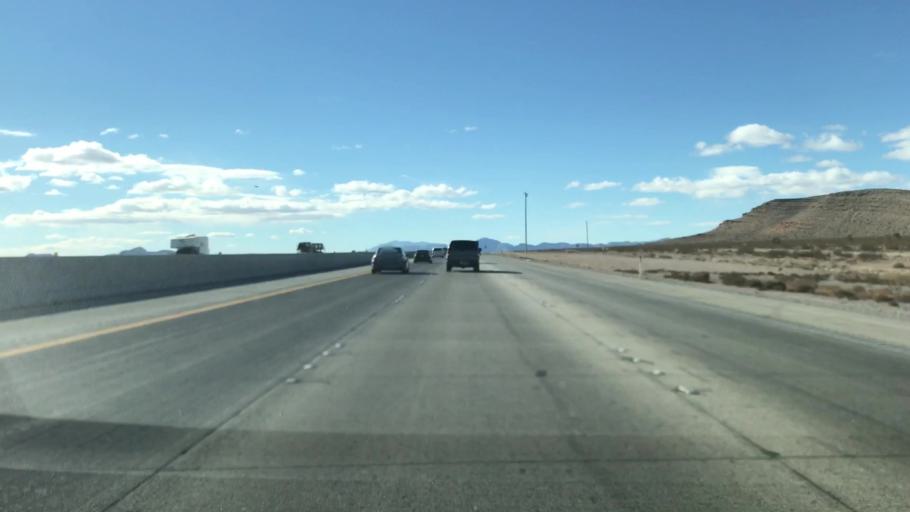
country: US
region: Nevada
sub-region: Clark County
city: Enterprise
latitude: 35.8785
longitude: -115.2345
